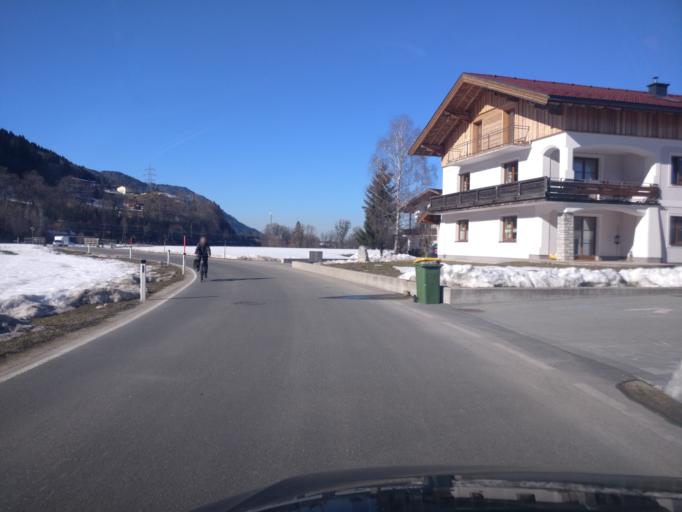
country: AT
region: Salzburg
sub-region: Politischer Bezirk Hallein
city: Kuchl
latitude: 47.6165
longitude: 13.1420
